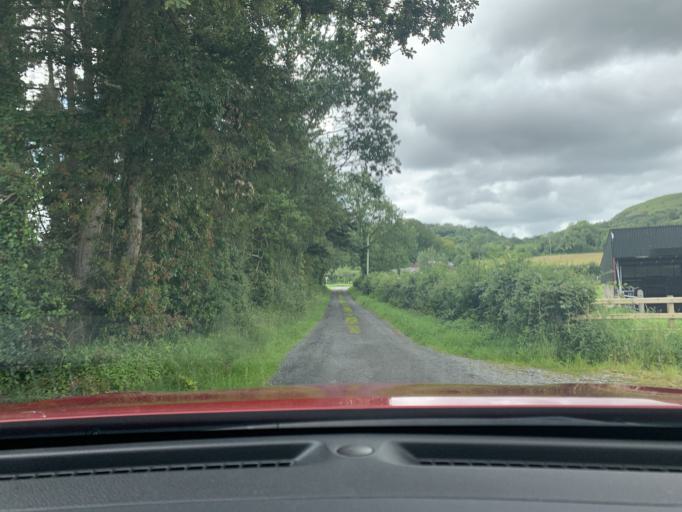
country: GB
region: Northern Ireland
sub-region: Fermanagh District
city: Enniskillen
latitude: 54.2729
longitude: -7.8073
